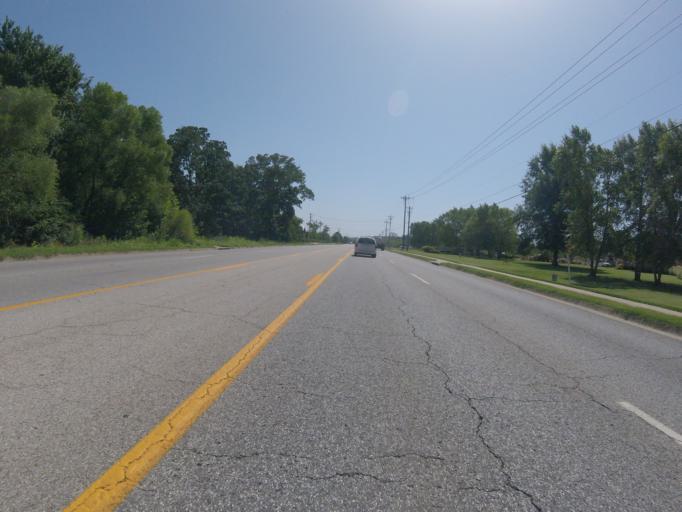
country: US
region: Arkansas
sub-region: Washington County
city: Farmington
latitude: 36.0785
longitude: -94.2128
